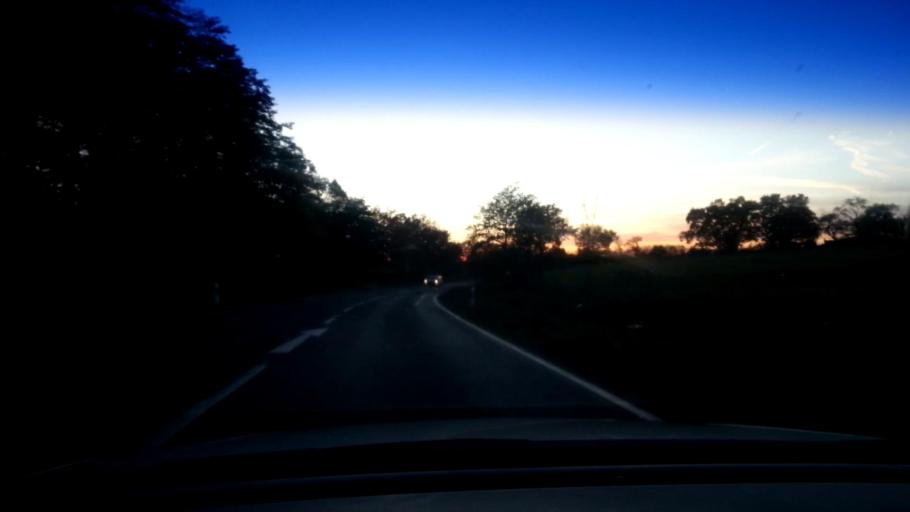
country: DE
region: Bavaria
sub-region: Upper Franconia
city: Litzendorf
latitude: 49.8706
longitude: 11.0318
